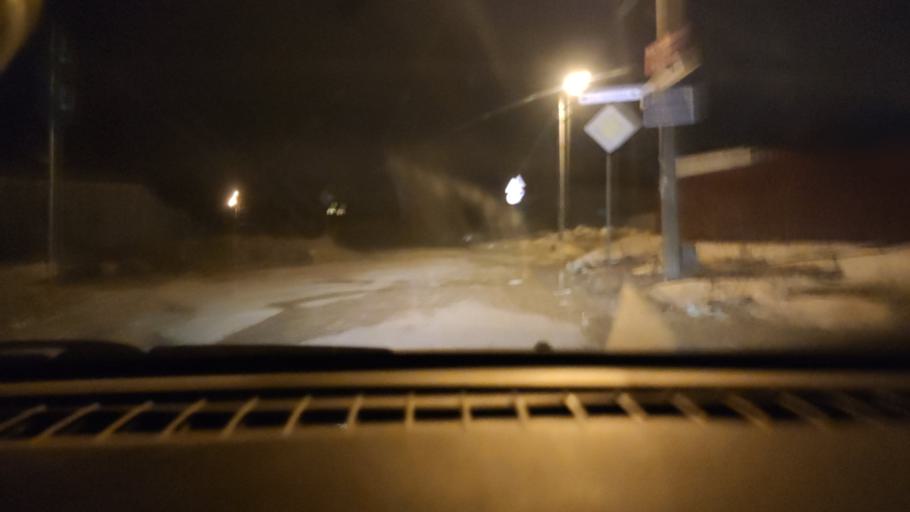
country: RU
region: Perm
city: Perm
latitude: 58.0825
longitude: 56.3539
